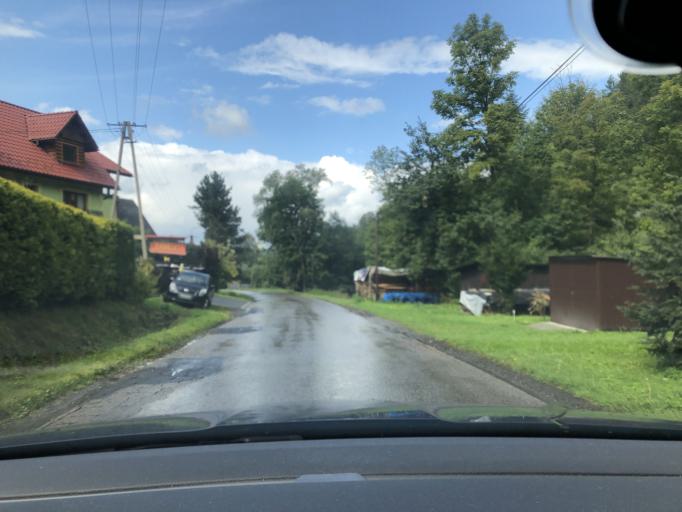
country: PL
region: Lesser Poland Voivodeship
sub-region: Powiat suski
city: Stryszawa
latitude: 49.7045
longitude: 19.5382
